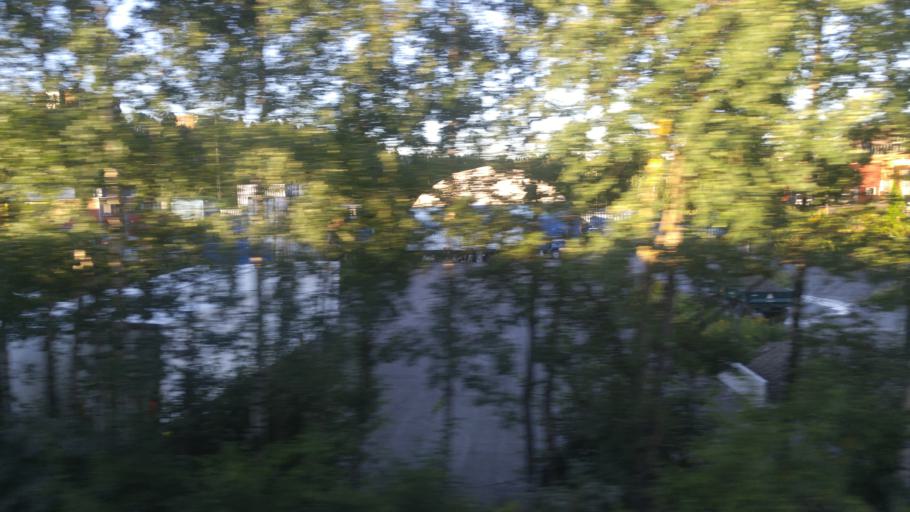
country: NO
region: Akershus
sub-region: Lorenskog
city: Kjenn
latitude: 59.9537
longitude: 10.8993
